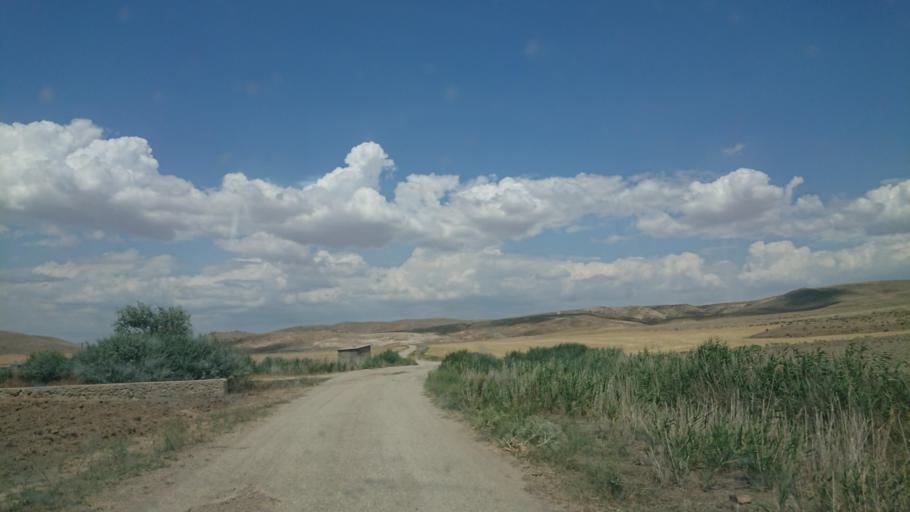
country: TR
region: Aksaray
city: Sariyahsi
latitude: 38.9905
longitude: 33.9105
